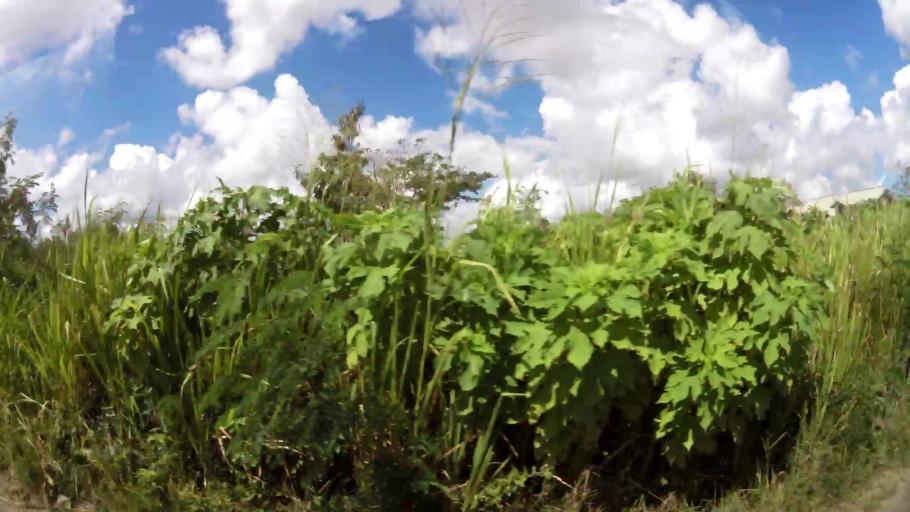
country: SR
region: Paramaribo
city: Paramaribo
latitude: 5.8657
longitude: -55.1311
